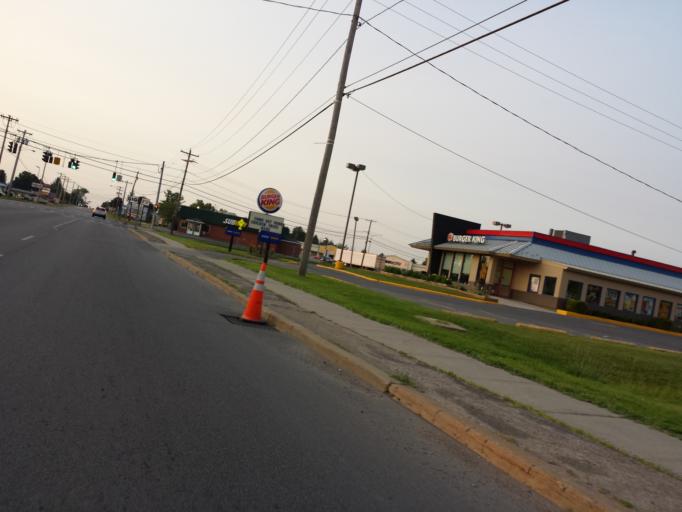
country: US
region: New York
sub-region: St. Lawrence County
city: Potsdam
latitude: 44.6829
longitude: -74.9869
